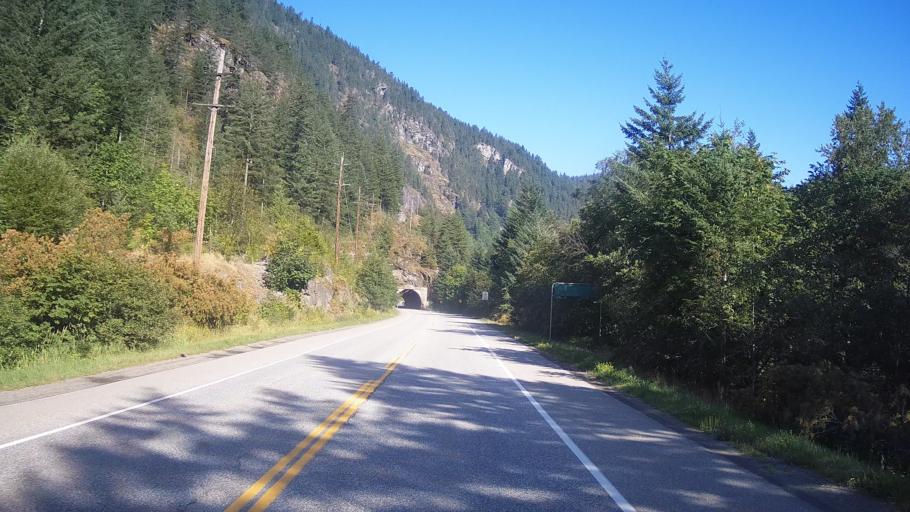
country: CA
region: British Columbia
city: Hope
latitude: 49.6349
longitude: -121.3988
